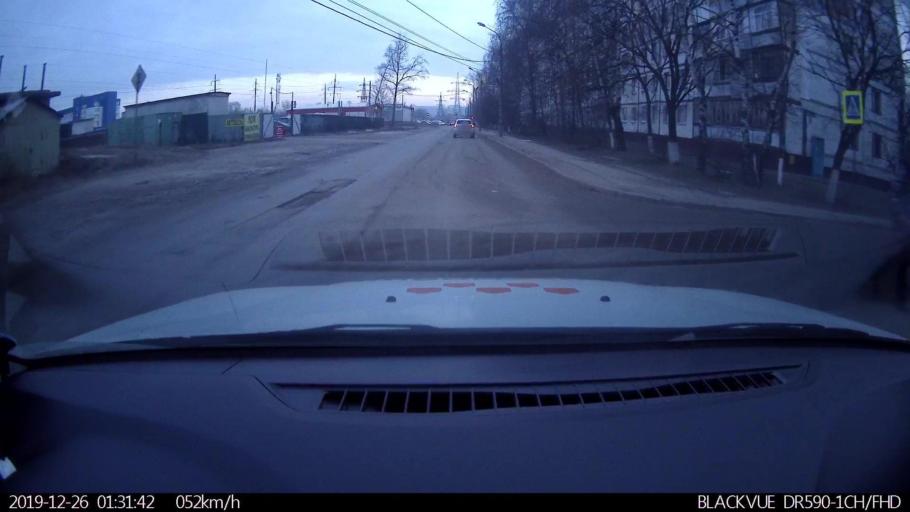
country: RU
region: Nizjnij Novgorod
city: Nizhniy Novgorod
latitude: 56.2658
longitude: 43.9011
